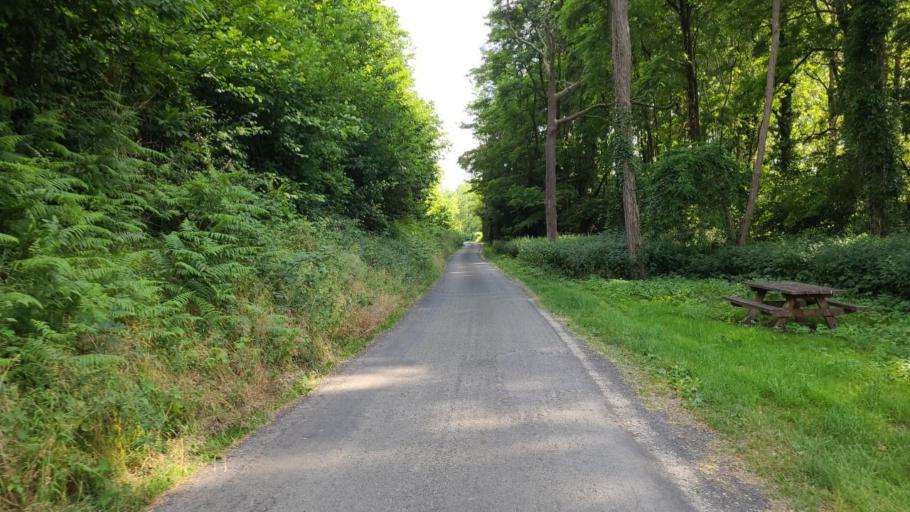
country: FR
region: Centre
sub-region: Departement d'Indre-et-Loire
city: Reugny
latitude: 47.4776
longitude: 0.8894
